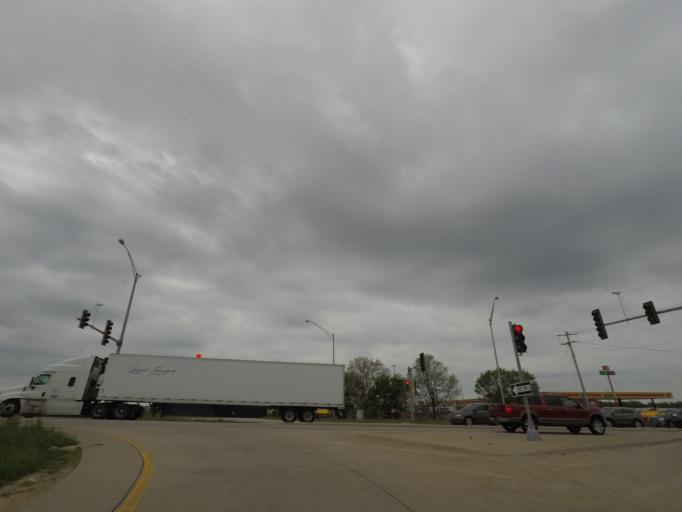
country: US
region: Illinois
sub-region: Winnebago County
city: Roscoe
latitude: 42.4571
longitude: -88.9972
